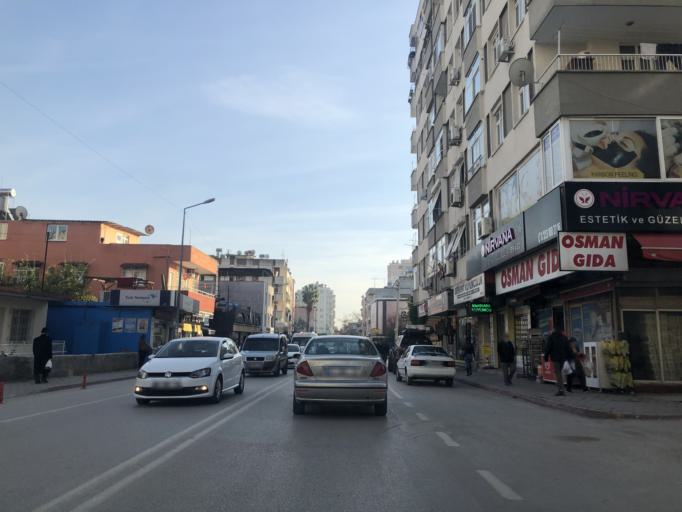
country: TR
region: Adana
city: Adana
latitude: 37.0210
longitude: 35.3138
